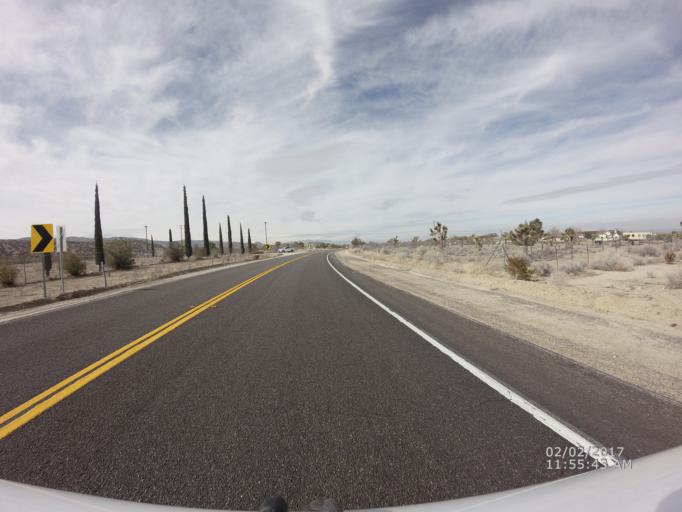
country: US
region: California
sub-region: Los Angeles County
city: Littlerock
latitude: 34.4922
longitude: -117.9438
